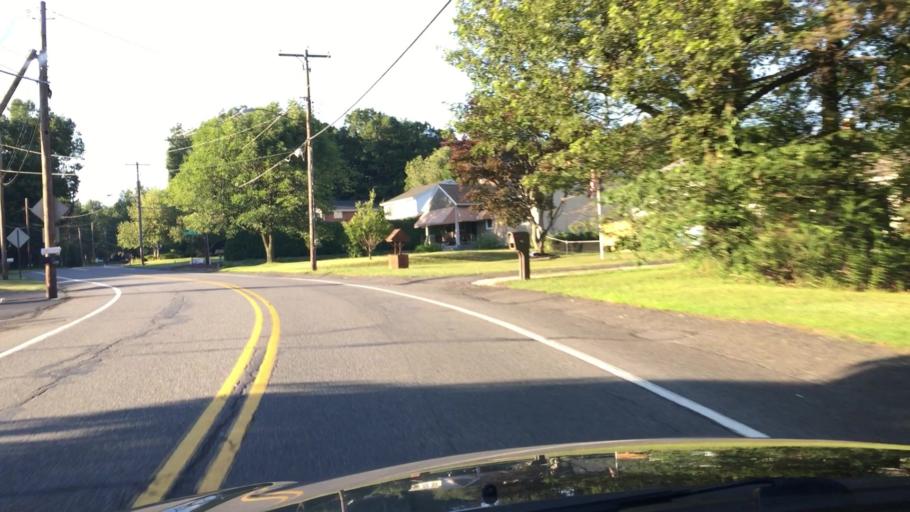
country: US
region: Pennsylvania
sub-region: Luzerne County
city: Harleigh
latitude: 40.9817
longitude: -75.9753
